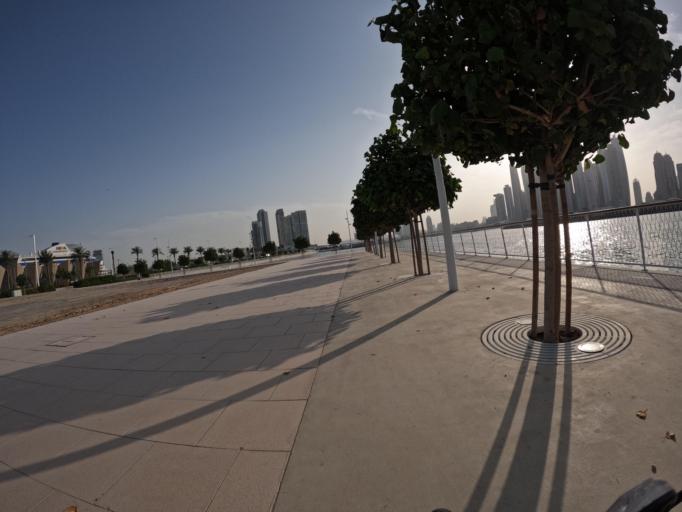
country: AE
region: Dubai
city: Dubai
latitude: 25.0922
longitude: 55.1323
